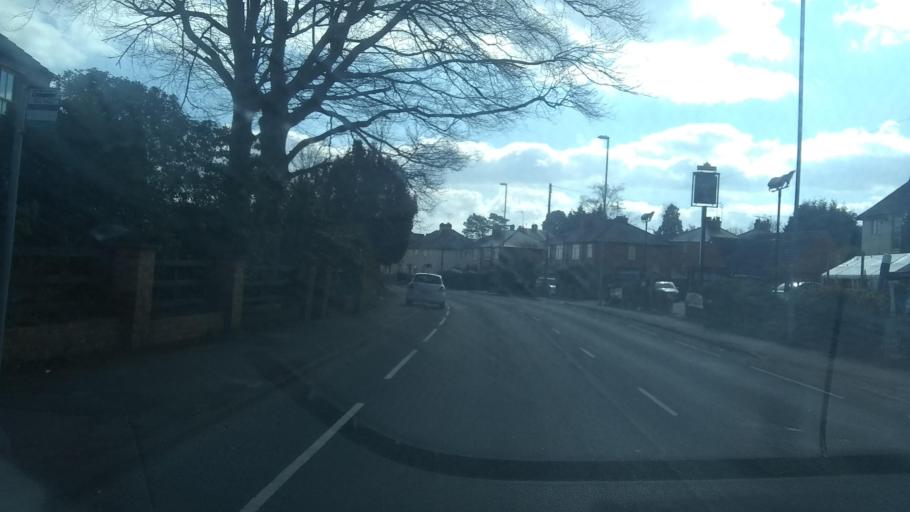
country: GB
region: England
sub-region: Worcestershire
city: Stourport-on-Severn
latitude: 52.3474
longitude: -2.2830
